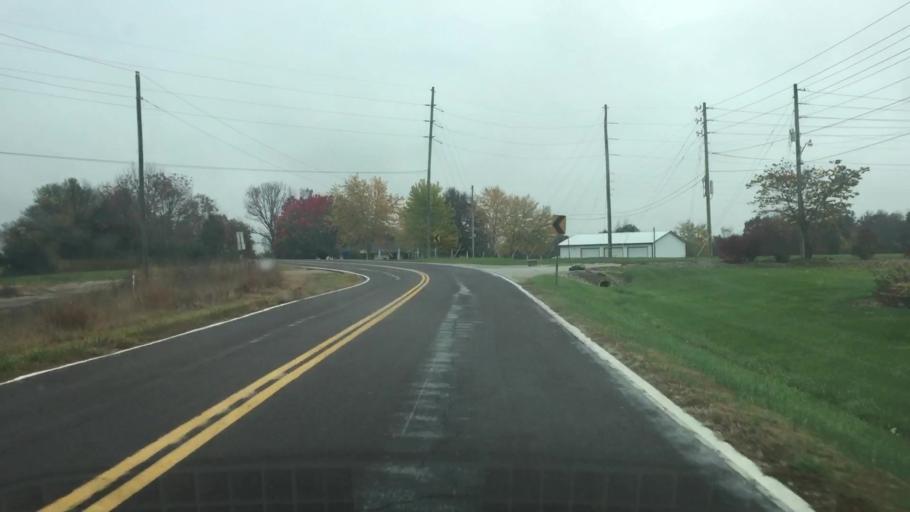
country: US
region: Missouri
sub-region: Callaway County
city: Fulton
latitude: 38.8394
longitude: -91.9225
